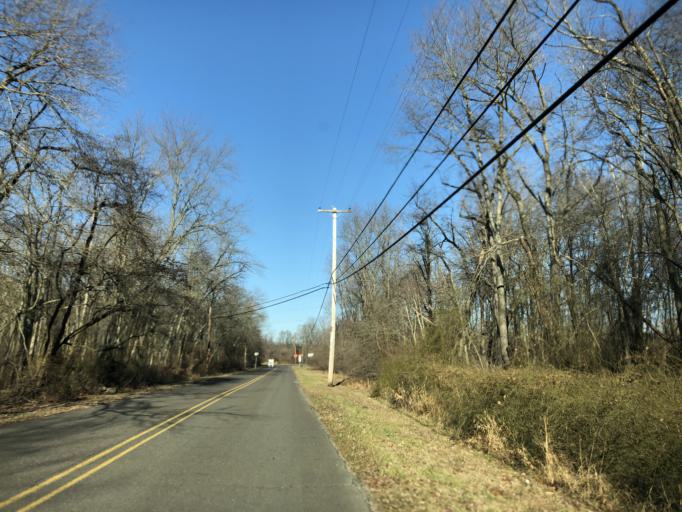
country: US
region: Pennsylvania
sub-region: Delaware County
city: Chester
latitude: 39.8064
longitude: -75.3558
